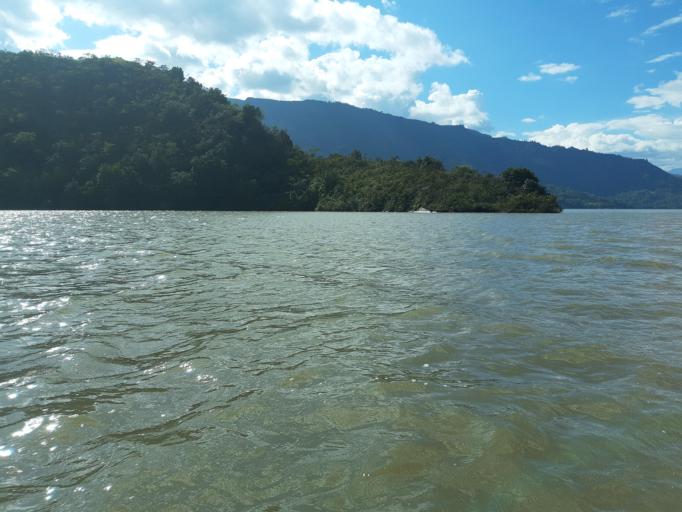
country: CO
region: Boyaca
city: Chivor
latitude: 4.9440
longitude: -73.3173
